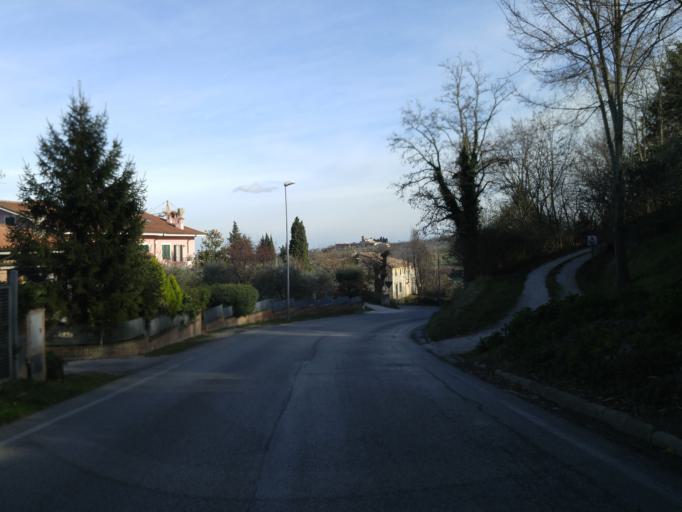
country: IT
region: The Marches
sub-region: Provincia di Pesaro e Urbino
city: Cartoceto
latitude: 43.7670
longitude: 12.8784
